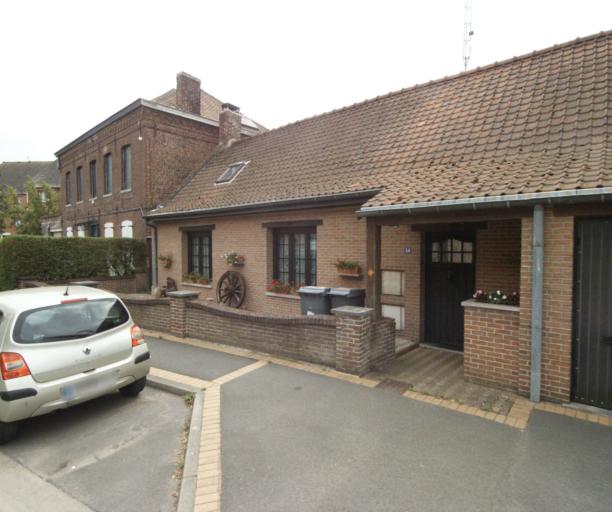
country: FR
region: Nord-Pas-de-Calais
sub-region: Departement du Nord
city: Leers
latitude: 50.6782
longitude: 3.2480
